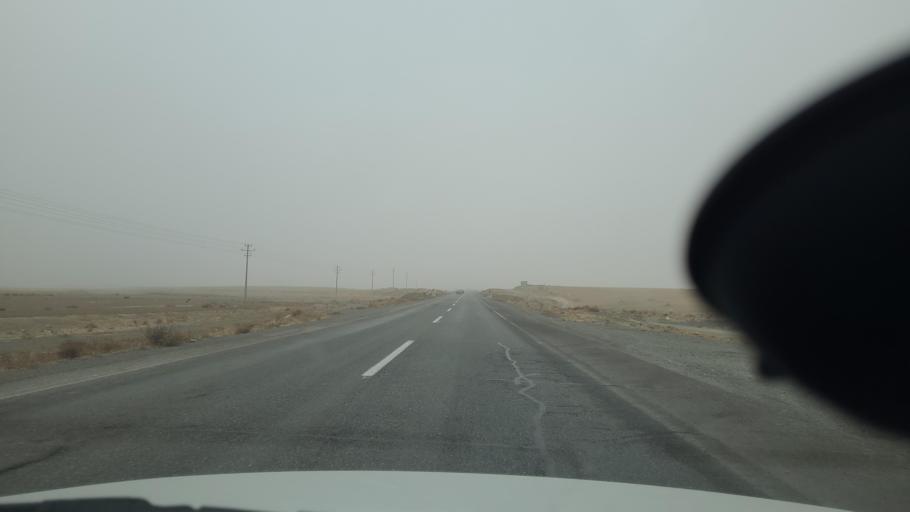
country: IR
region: Razavi Khorasan
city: Fariman
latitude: 35.7439
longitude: 59.7665
